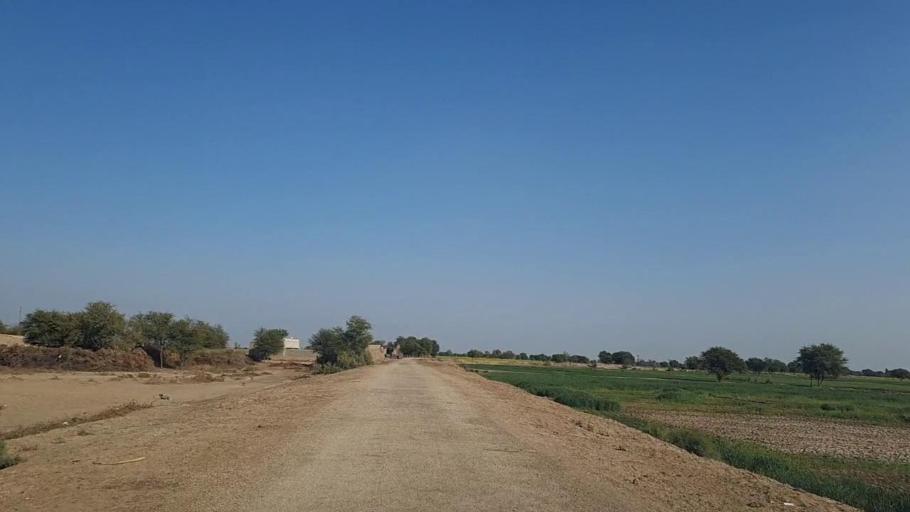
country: PK
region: Sindh
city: Shahpur Chakar
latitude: 26.2049
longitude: 68.6413
